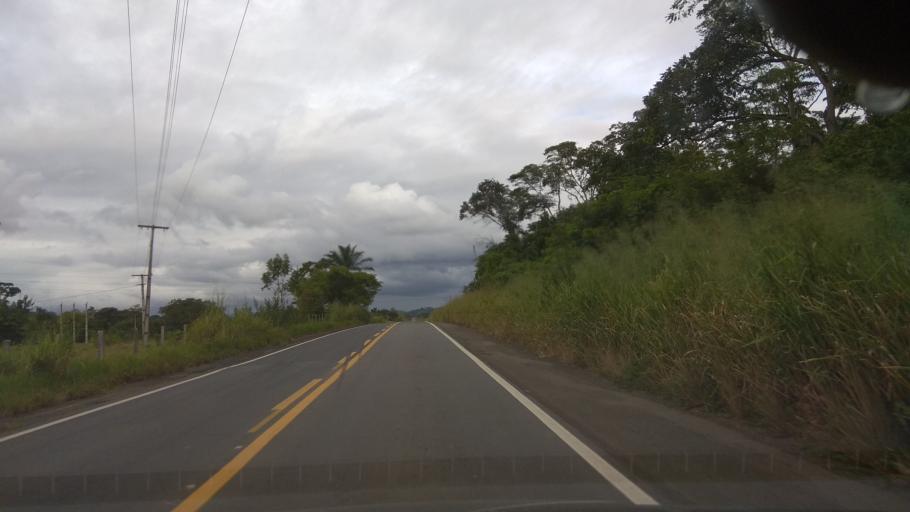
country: BR
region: Bahia
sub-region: Ipiau
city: Ipiau
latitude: -14.1940
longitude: -39.6470
